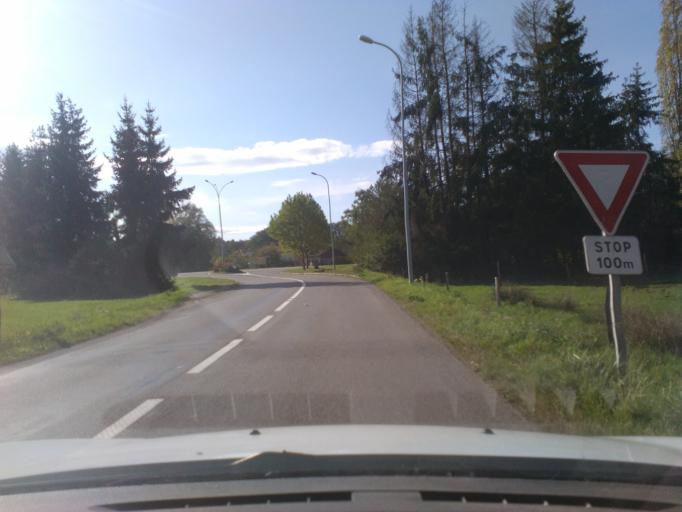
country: FR
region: Lorraine
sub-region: Departement des Vosges
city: Sainte-Marguerite
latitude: 48.2653
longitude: 6.9950
